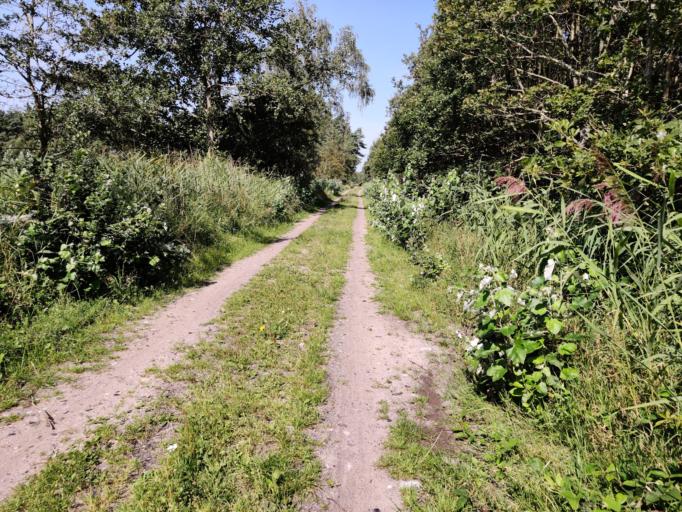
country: DK
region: Zealand
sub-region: Guldborgsund Kommune
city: Nykobing Falster
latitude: 54.6195
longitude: 11.9564
